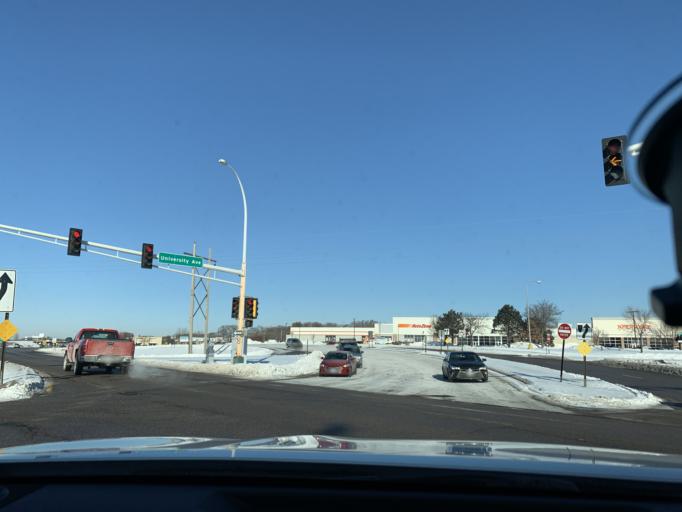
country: US
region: Minnesota
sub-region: Anoka County
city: Coon Rapids
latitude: 45.1313
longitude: -93.2638
